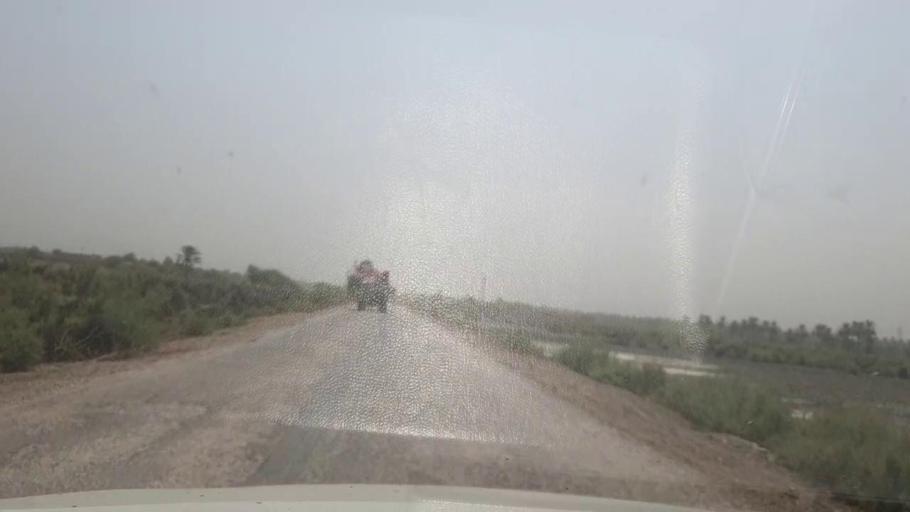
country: PK
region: Sindh
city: Kot Diji
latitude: 27.3765
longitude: 68.6983
